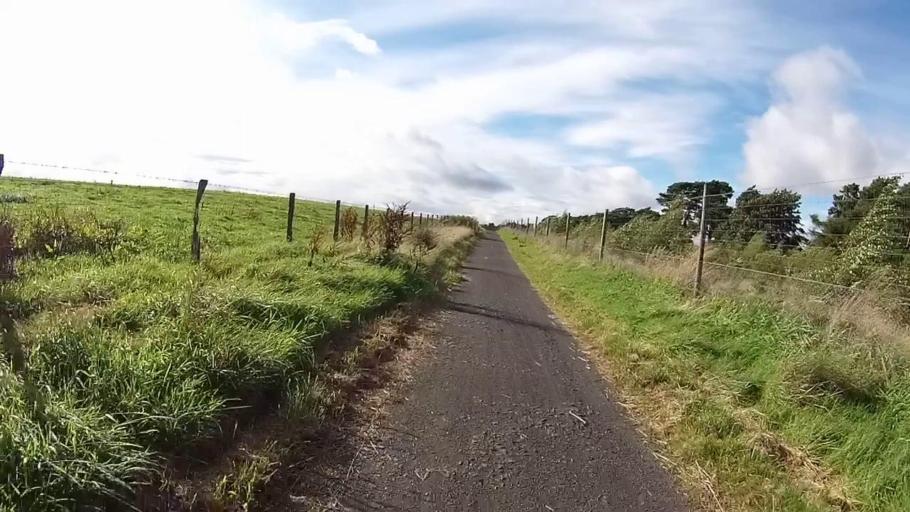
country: GB
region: Scotland
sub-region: Perth and Kinross
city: Kinross
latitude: 56.1892
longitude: -3.3986
